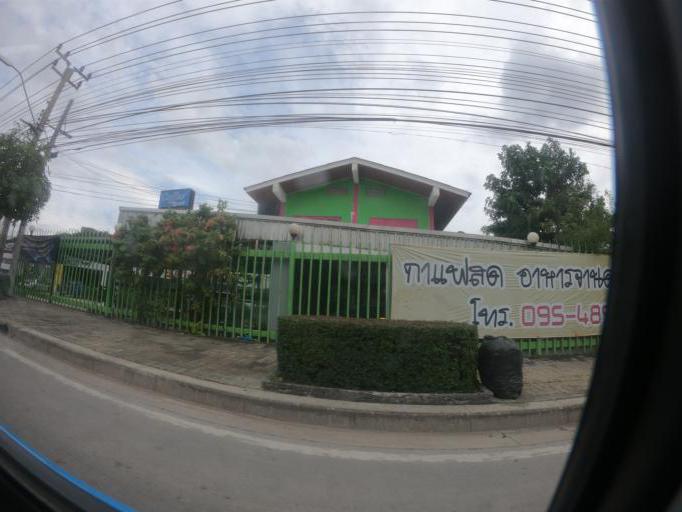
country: TH
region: Bangkok
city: Suan Luang
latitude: 13.7169
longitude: 100.6578
